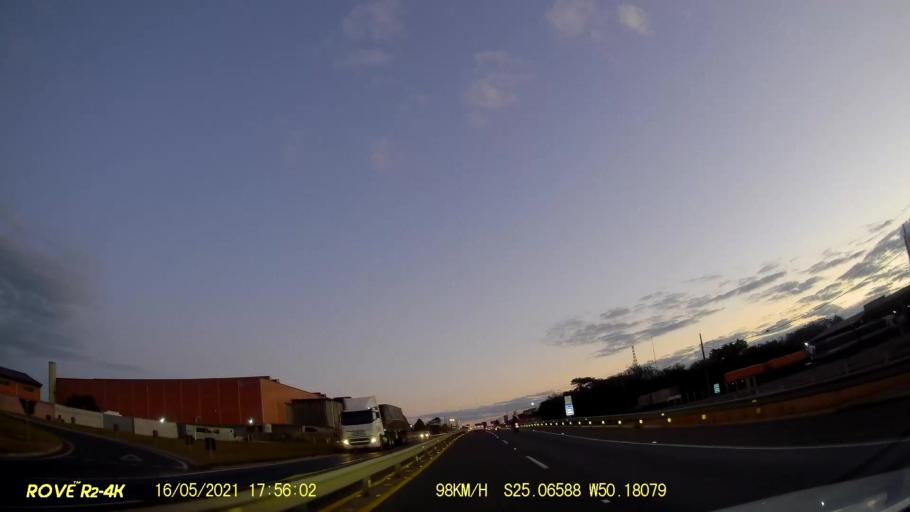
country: BR
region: Parana
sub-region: Ponta Grossa
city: Ponta Grossa
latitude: -25.0659
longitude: -50.1808
